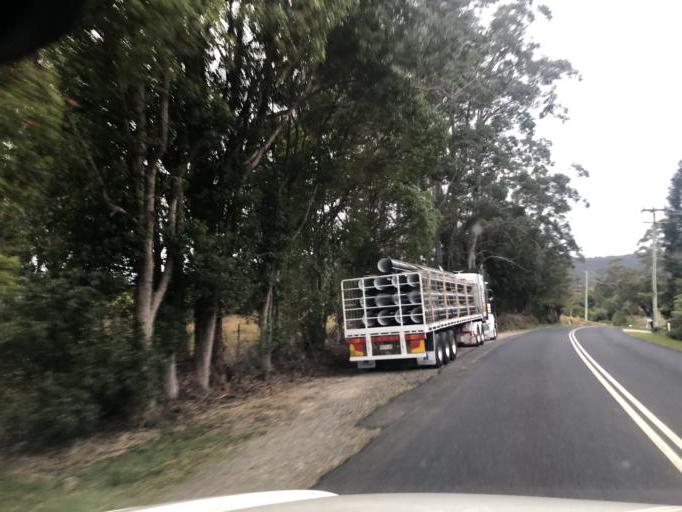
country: AU
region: New South Wales
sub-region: Coffs Harbour
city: Coffs Harbour
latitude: -30.2566
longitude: 153.0388
